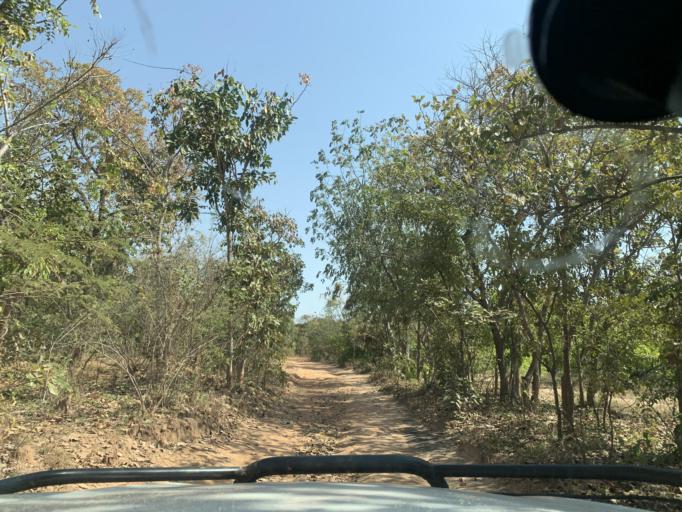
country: ML
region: Sikasso
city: Kolondieba
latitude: 10.8939
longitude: -6.7473
